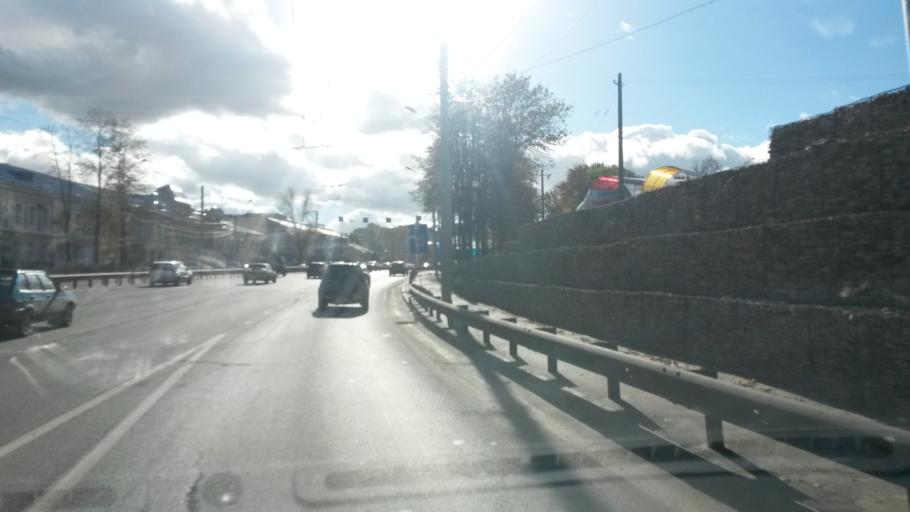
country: RU
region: Jaroslavl
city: Yaroslavl
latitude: 57.6018
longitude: 39.8765
